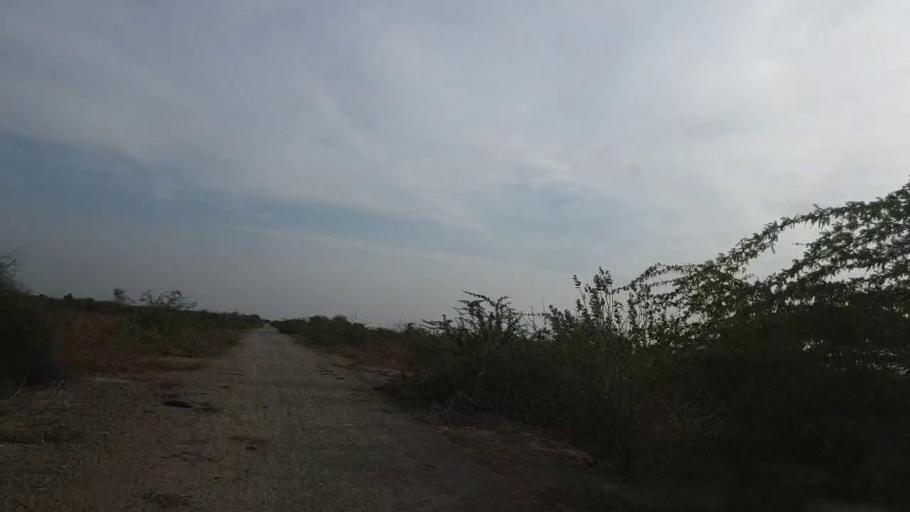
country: PK
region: Sindh
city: Nabisar
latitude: 24.9974
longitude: 69.5183
